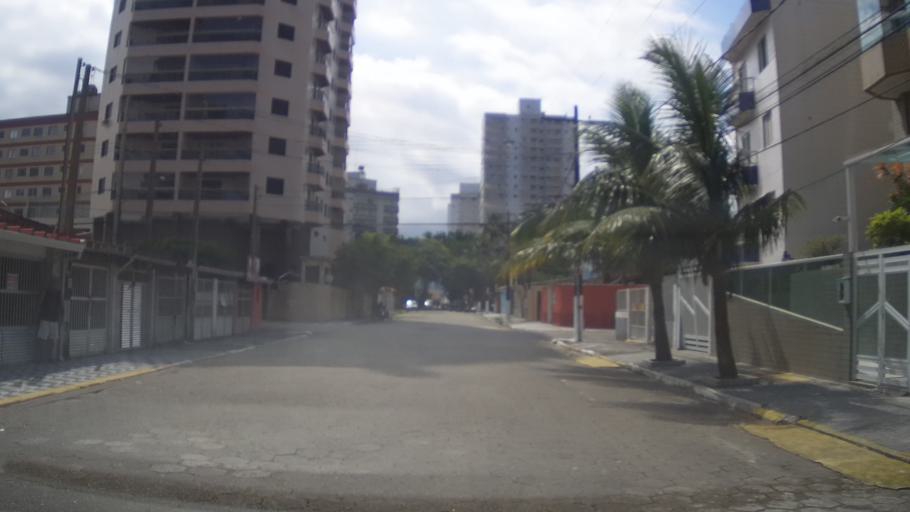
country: BR
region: Sao Paulo
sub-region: Praia Grande
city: Praia Grande
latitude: -24.0199
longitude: -46.4493
